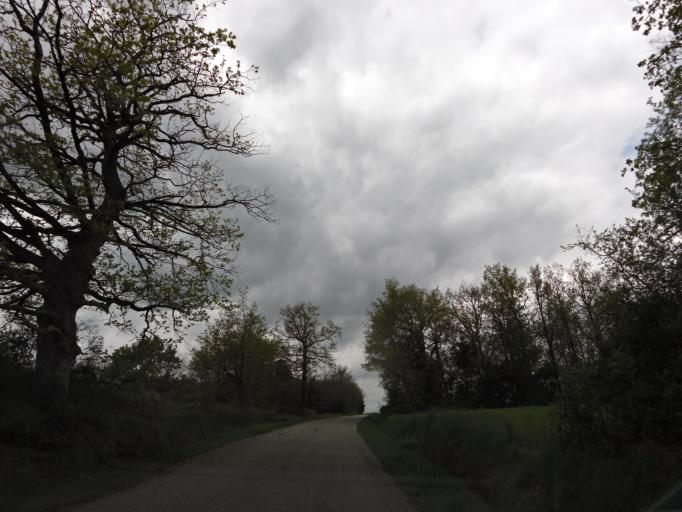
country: FR
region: Languedoc-Roussillon
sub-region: Departement de l'Aude
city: Saint-Martin-Lalande
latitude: 43.3484
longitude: 2.0603
